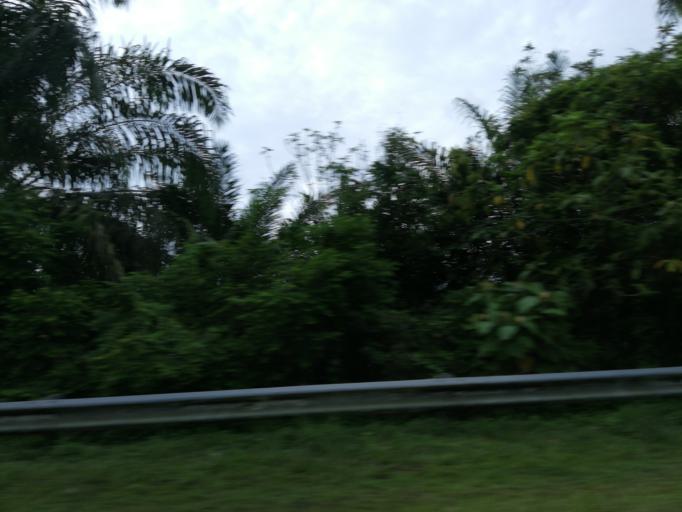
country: MY
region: Penang
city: Tasek Glugor
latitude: 5.5028
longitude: 100.6166
